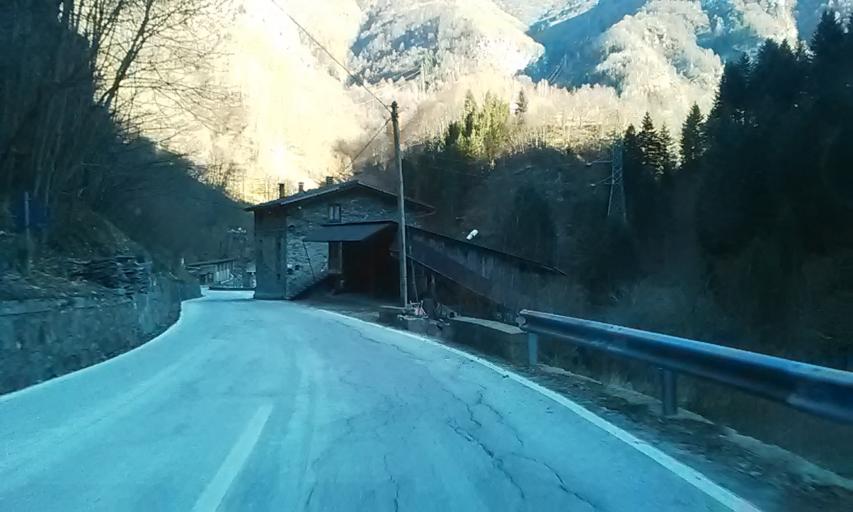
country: IT
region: Piedmont
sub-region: Provincia di Vercelli
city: Rimasco
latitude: 45.8418
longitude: 8.0743
